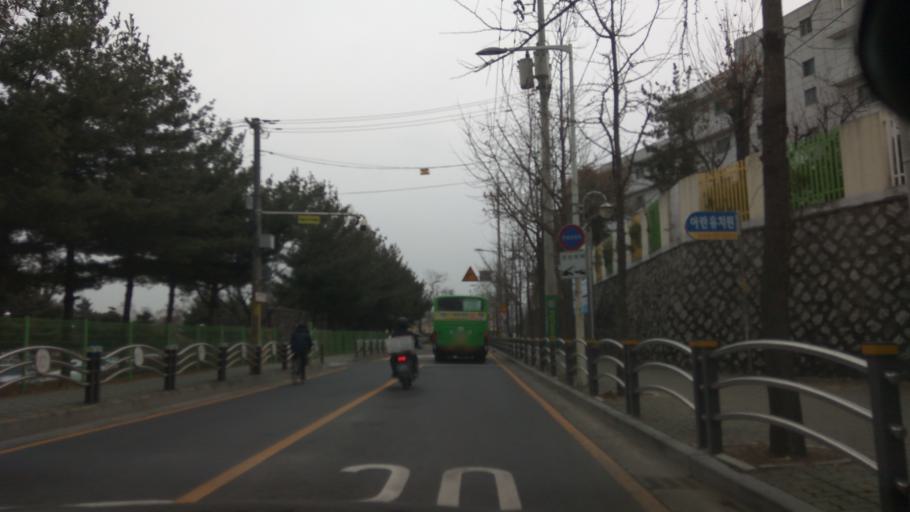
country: KR
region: Incheon
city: Incheon
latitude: 37.4945
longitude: 126.7088
